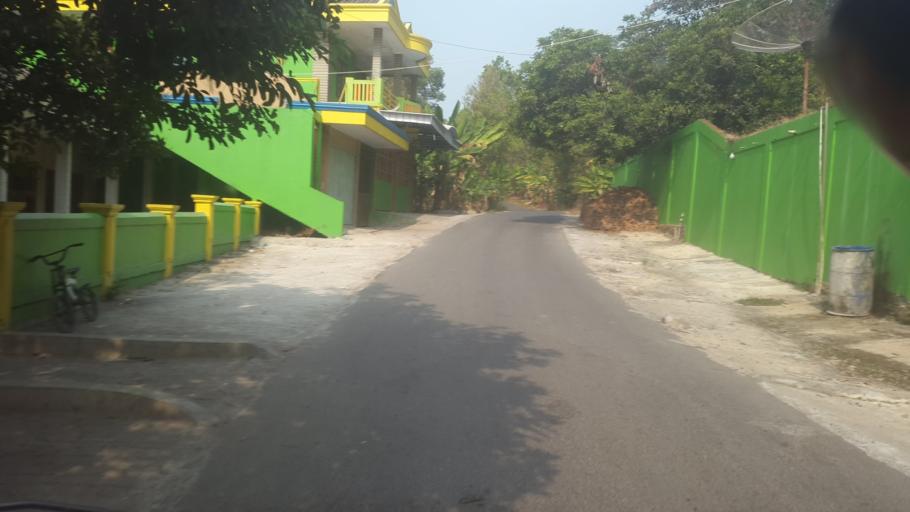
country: ID
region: West Java
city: Pelabuhanratu
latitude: -6.9549
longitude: 106.5349
